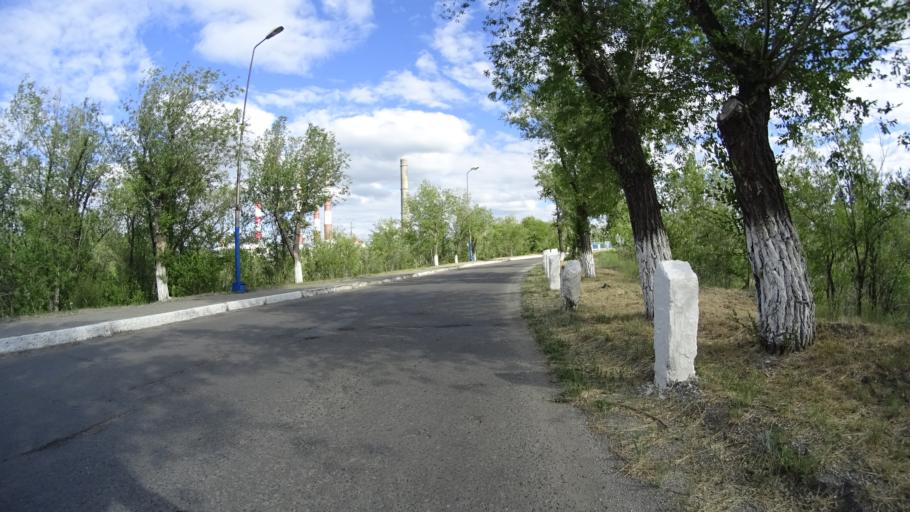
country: RU
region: Chelyabinsk
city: Troitsk
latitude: 54.0405
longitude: 61.6391
